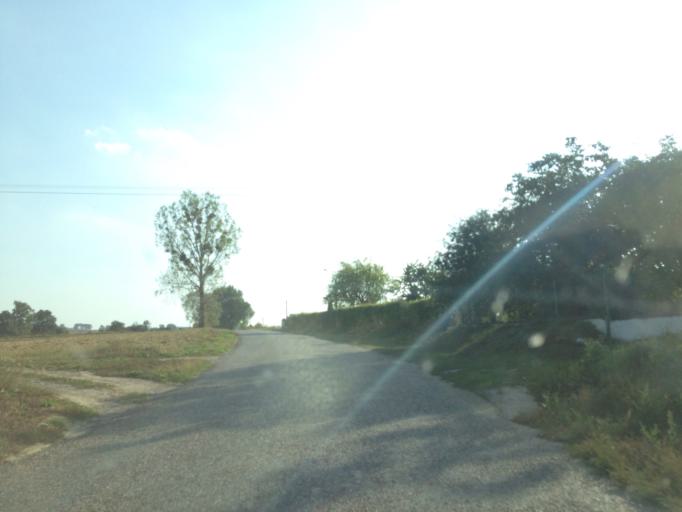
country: PL
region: Warmian-Masurian Voivodeship
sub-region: Powiat nowomiejski
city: Biskupiec
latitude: 53.4465
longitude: 19.2984
